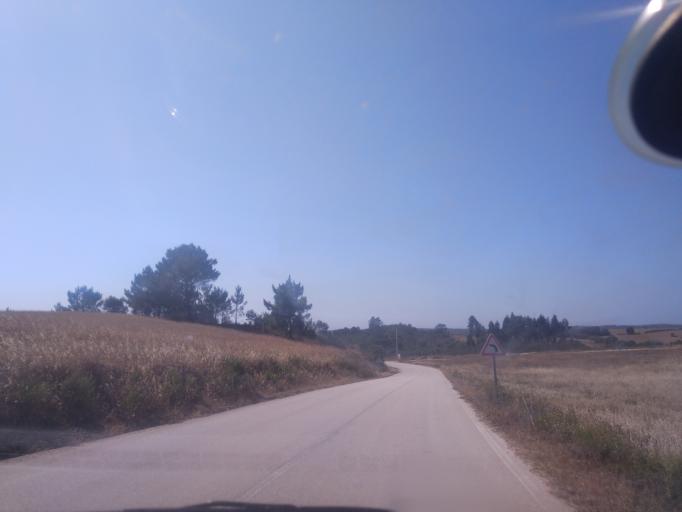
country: PT
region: Faro
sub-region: Aljezur
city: Aljezur
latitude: 37.2263
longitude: -8.8154
